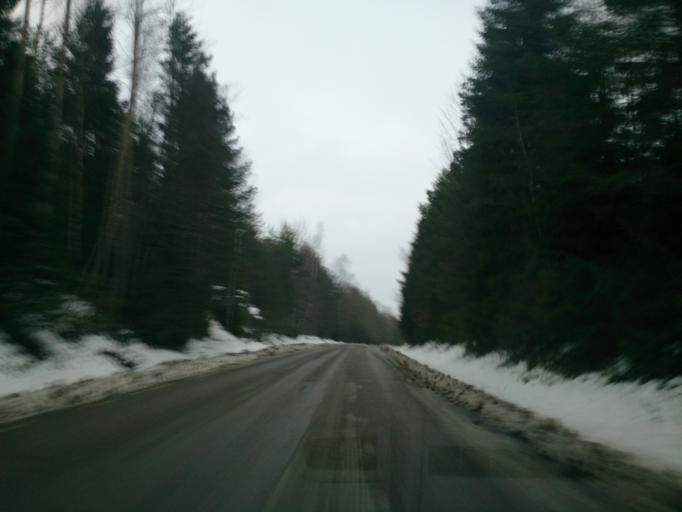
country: SE
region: OEstergoetland
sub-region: Atvidabergs Kommun
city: Atvidaberg
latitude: 58.2527
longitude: 16.0197
